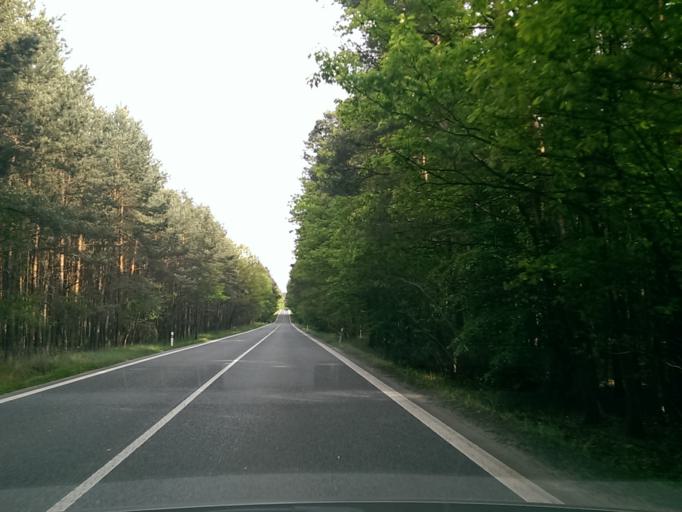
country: CZ
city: Doksy
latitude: 50.5368
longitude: 14.6836
